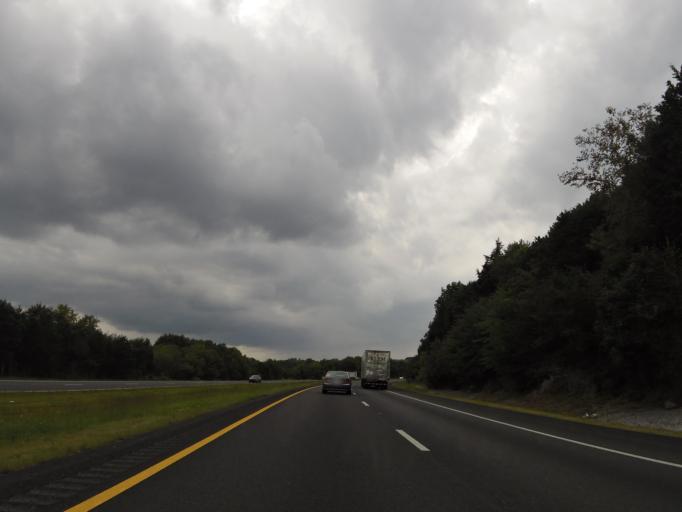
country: US
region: Tennessee
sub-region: Wilson County
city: Watertown
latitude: 36.1665
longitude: -86.1013
